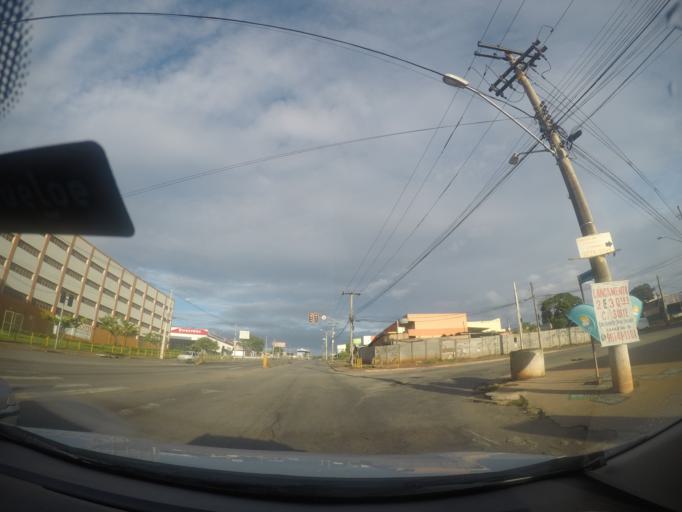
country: BR
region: Goias
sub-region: Goiania
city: Goiania
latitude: -16.6647
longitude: -49.3183
